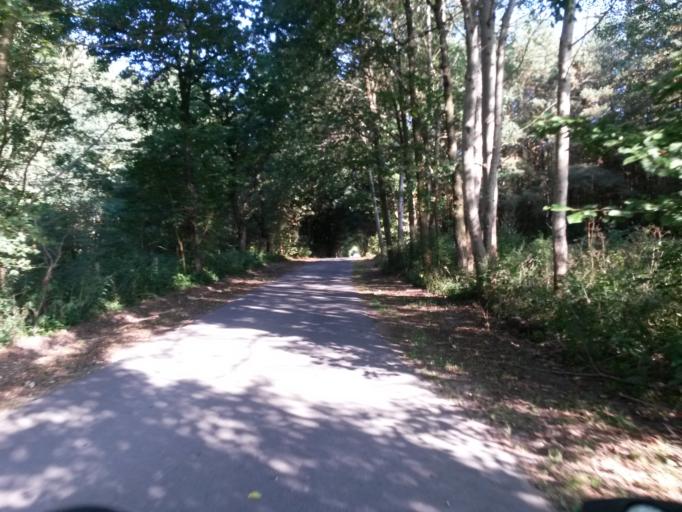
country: DE
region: Brandenburg
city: Templin
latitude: 53.1332
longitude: 13.4516
